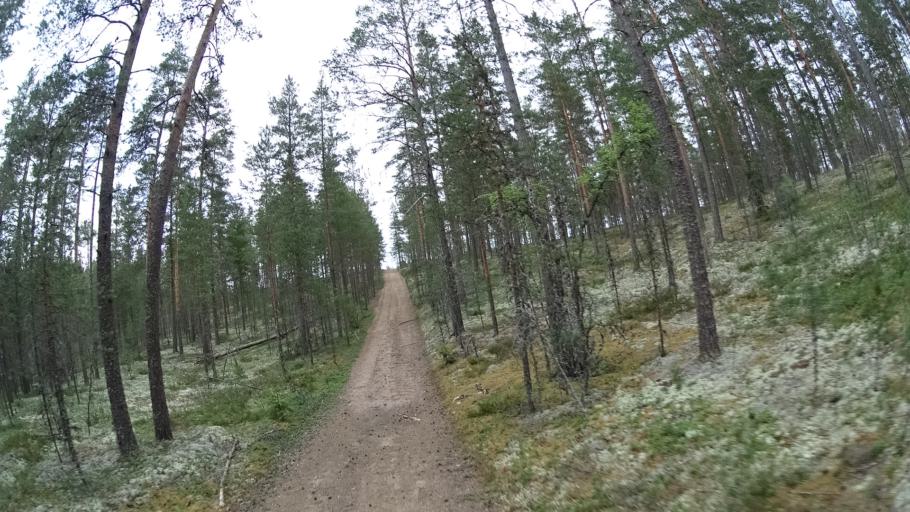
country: FI
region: Satakunta
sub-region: Pohjois-Satakunta
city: Jaemijaervi
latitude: 61.7687
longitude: 22.7906
